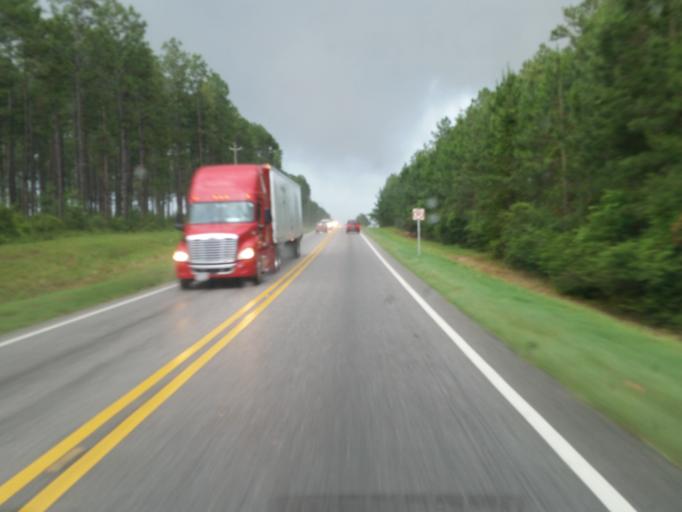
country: US
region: Alabama
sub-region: Mobile County
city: Chickasaw
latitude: 30.7870
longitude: -88.2855
